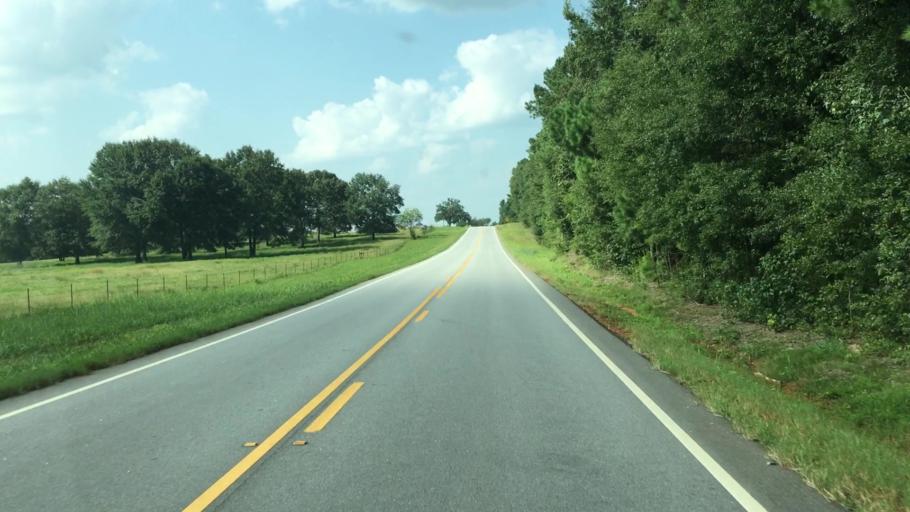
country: US
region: Georgia
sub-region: Newton County
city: Covington
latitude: 33.4634
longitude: -83.7534
